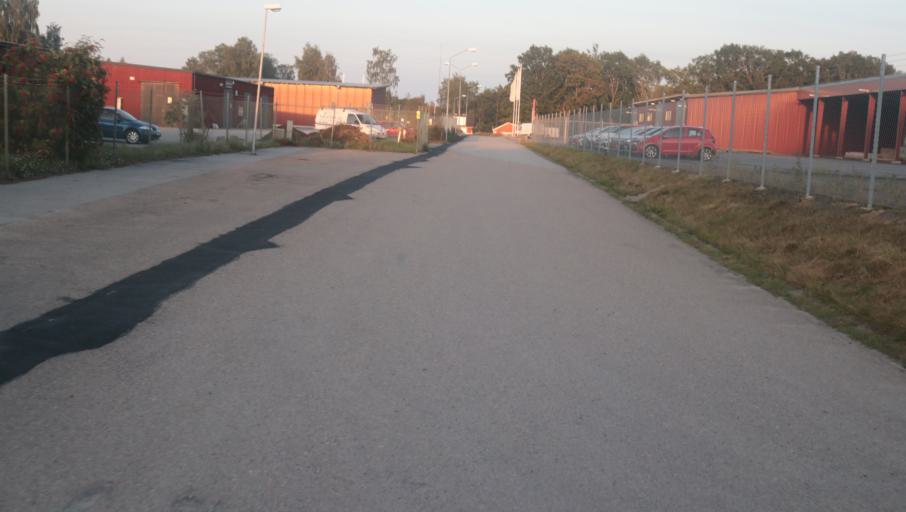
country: SE
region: Blekinge
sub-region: Karlshamns Kommun
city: Karlshamn
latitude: 56.2215
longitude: 14.8219
